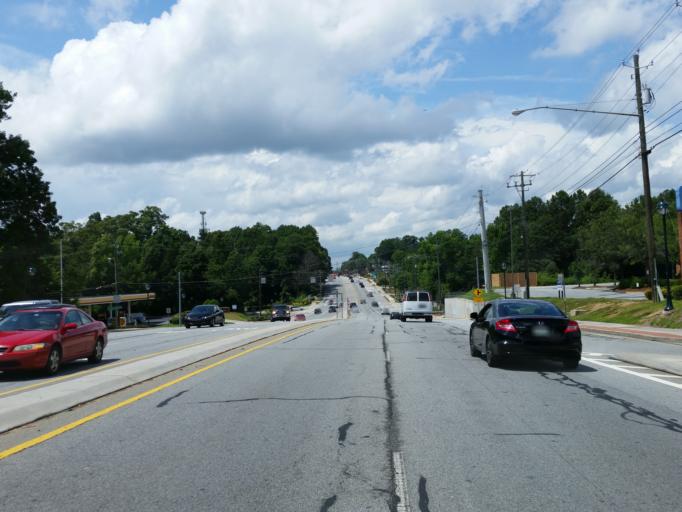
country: US
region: Georgia
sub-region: DeKalb County
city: Dunwoody
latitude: 33.9819
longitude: -84.3502
